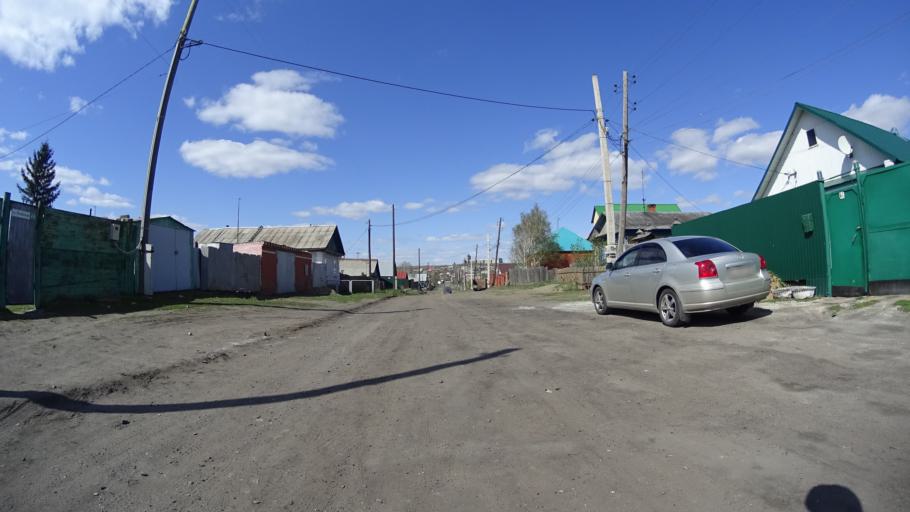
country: RU
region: Chelyabinsk
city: Troitsk
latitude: 54.0900
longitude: 61.5950
